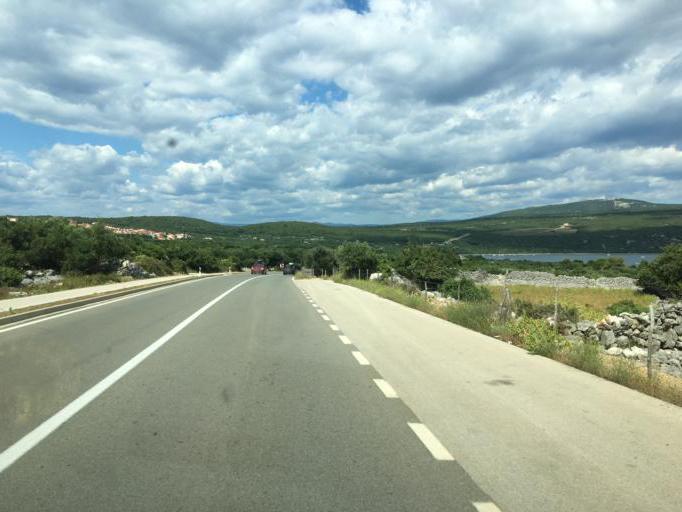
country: HR
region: Primorsko-Goranska
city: Punat
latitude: 45.0338
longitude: 14.6058
